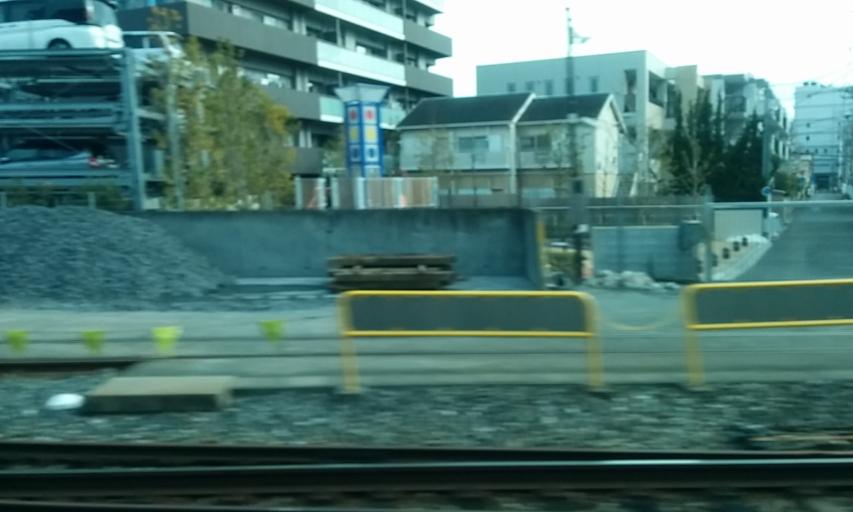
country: JP
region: Saitama
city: Kawaguchi
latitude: 35.8051
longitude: 139.7149
